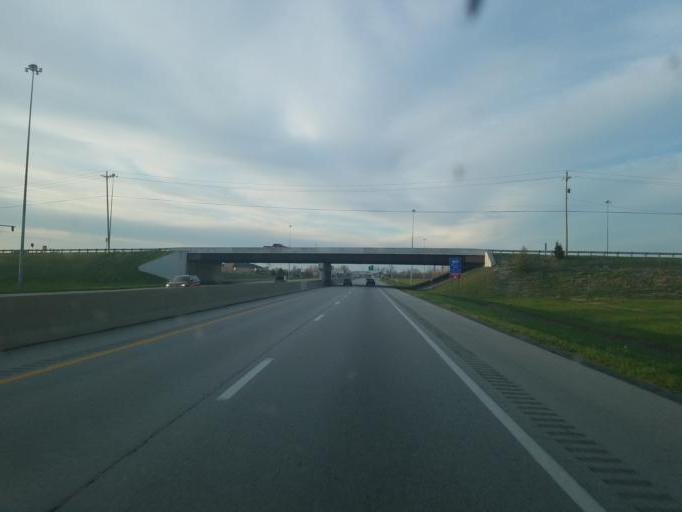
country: US
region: Ohio
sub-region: Wood County
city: Northwood
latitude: 41.6152
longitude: -83.4769
